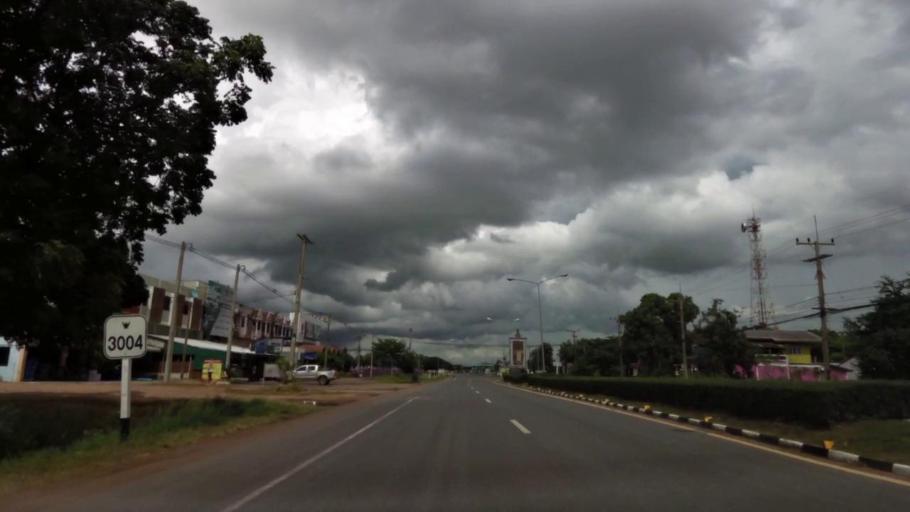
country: TH
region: Nakhon Sawan
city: Phai Sali
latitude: 15.5942
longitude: 100.6566
